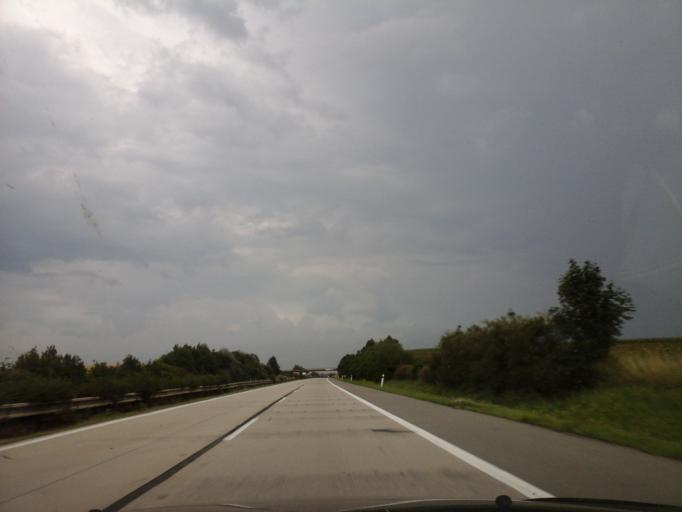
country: CZ
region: South Moravian
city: Rajhradice
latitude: 49.1094
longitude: 16.6513
